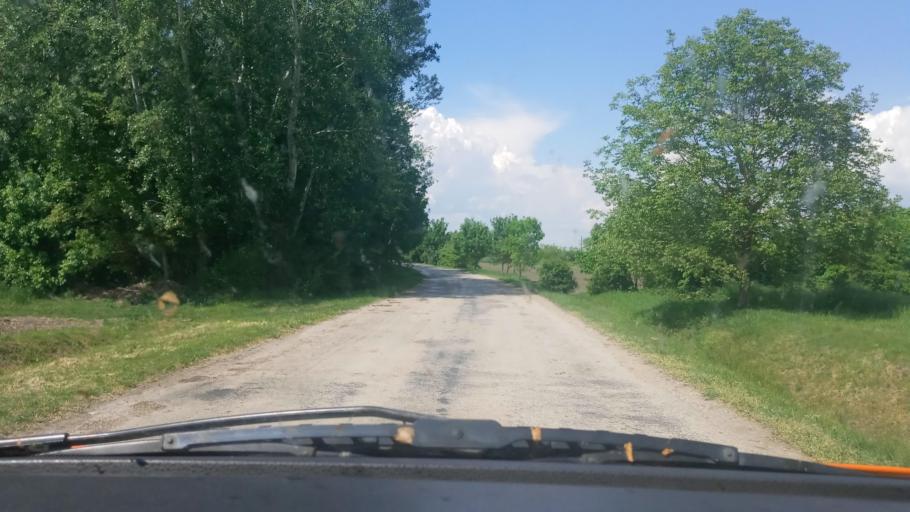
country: HU
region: Baranya
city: Siklos
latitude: 45.7959
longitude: 18.3501
